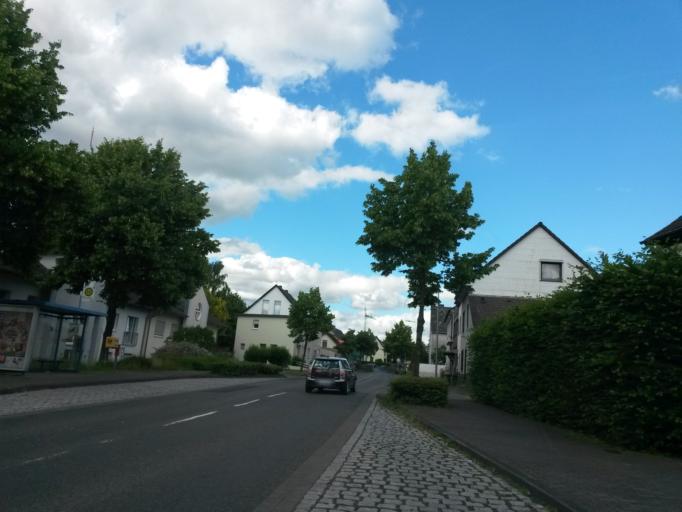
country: DE
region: North Rhine-Westphalia
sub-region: Regierungsbezirk Koln
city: Hennef
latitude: 50.8257
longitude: 7.2788
